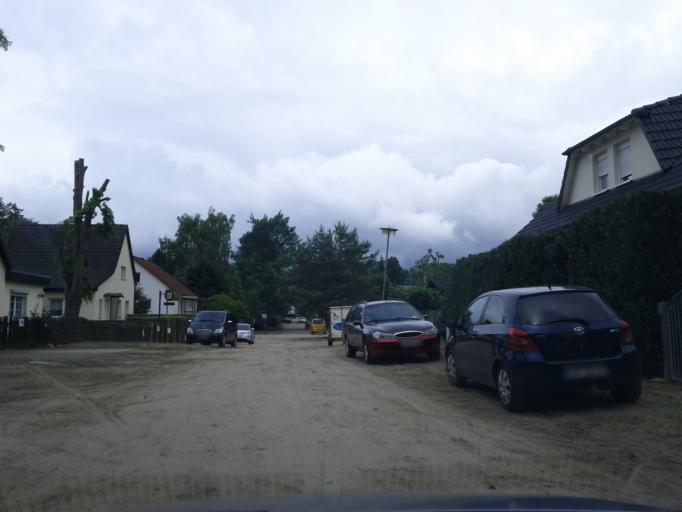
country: DE
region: Brandenburg
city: Woltersdorf
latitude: 52.4534
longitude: 13.7501
